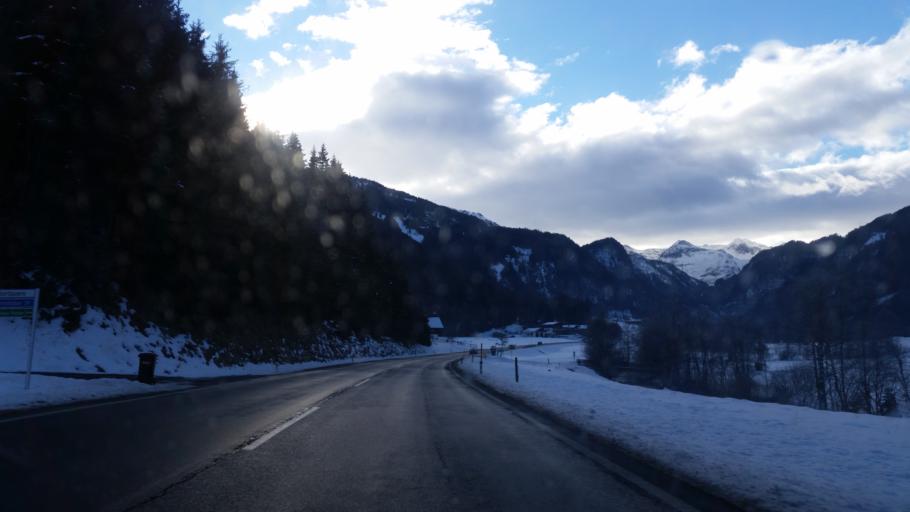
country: AT
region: Salzburg
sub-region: Politischer Bezirk Sankt Johann im Pongau
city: Untertauern
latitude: 47.3252
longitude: 13.5083
